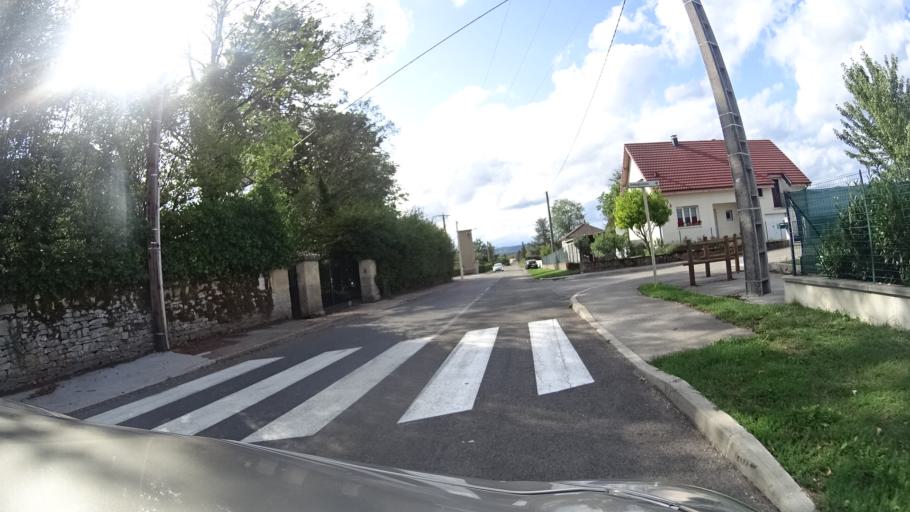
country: FR
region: Franche-Comte
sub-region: Departement du Doubs
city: Mamirolle
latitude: 47.2022
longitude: 6.1567
